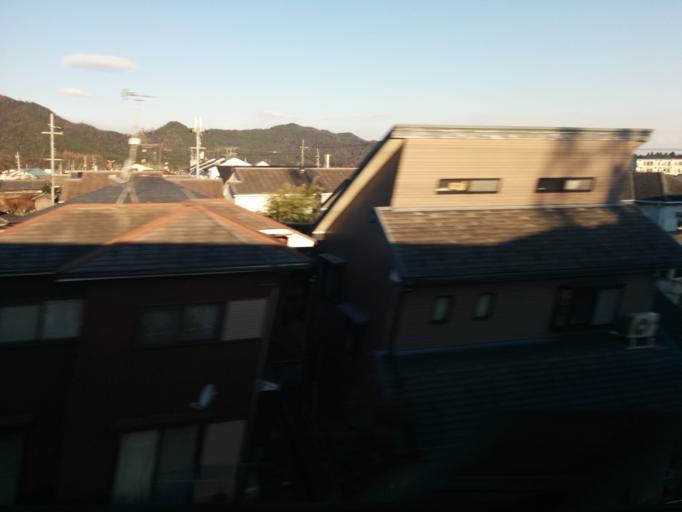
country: JP
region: Shiga Prefecture
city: Youkaichi
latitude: 35.1438
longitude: 136.1839
